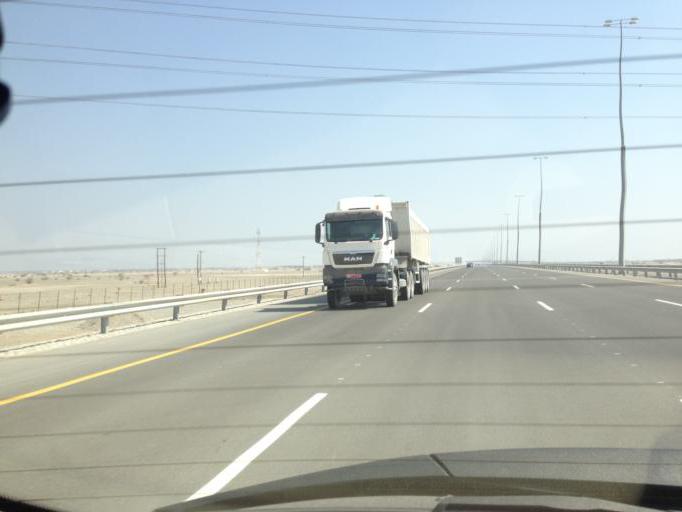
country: OM
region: Al Batinah
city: Barka'
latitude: 23.6118
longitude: 57.8303
